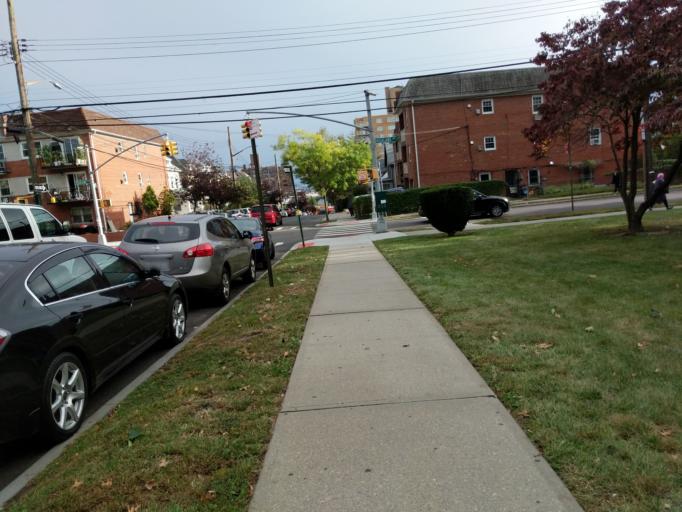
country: US
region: New York
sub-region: Queens County
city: Jamaica
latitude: 40.7117
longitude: -73.7967
